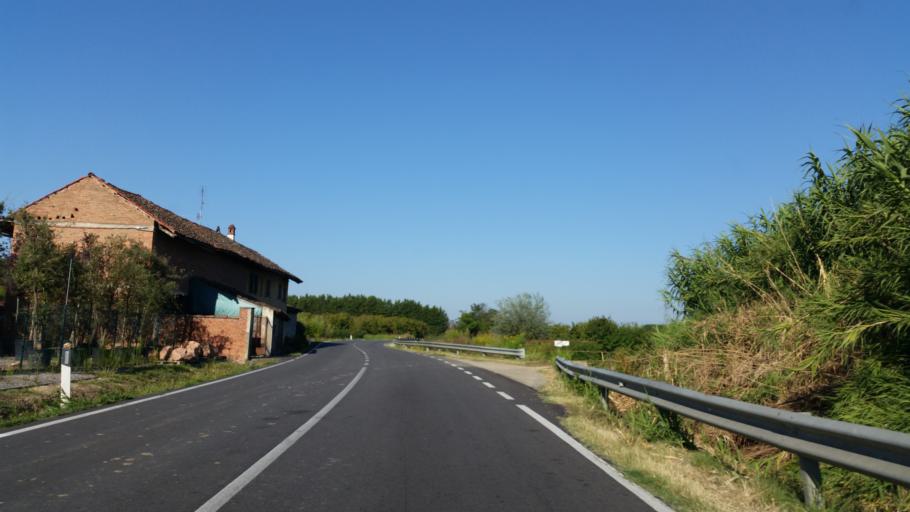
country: IT
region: Piedmont
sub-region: Provincia di Cuneo
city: Roddi
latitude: 44.6851
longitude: 7.9641
